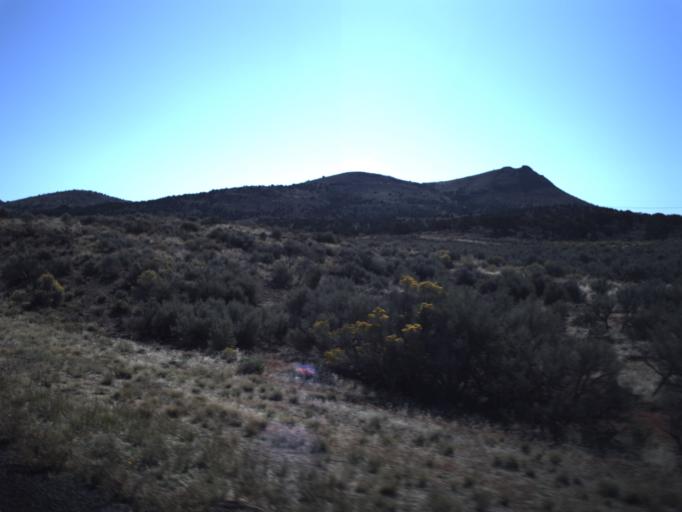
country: US
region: Utah
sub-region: Washington County
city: Enterprise
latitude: 37.6746
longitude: -113.5247
